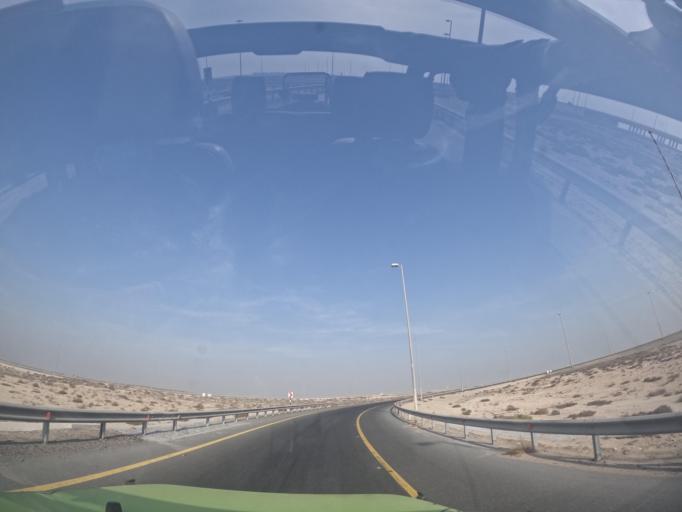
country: AE
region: Dubai
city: Dubai
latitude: 24.8533
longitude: 55.0075
